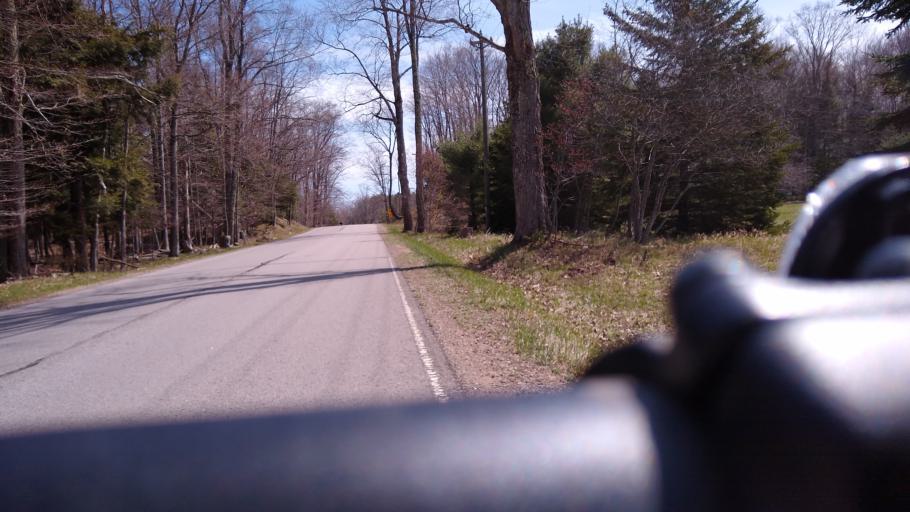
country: US
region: Michigan
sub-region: Delta County
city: Escanaba
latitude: 45.6978
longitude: -87.1629
